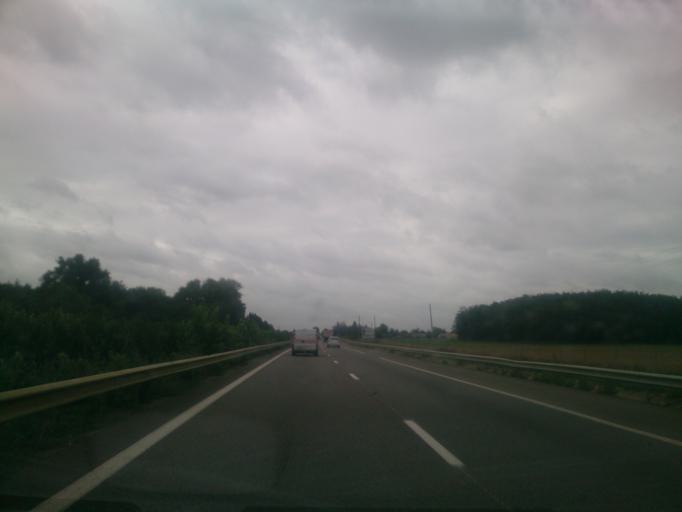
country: FR
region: Midi-Pyrenees
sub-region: Departement de la Haute-Garonne
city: Le Fauga
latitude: 43.4146
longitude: 1.2975
